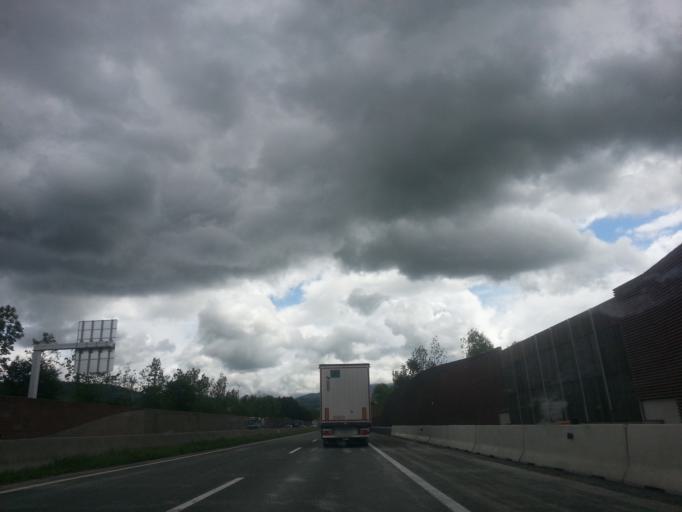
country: AT
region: Salzburg
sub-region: Politischer Bezirk Salzburg-Umgebung
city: Grodig
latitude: 47.7446
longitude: 13.0369
